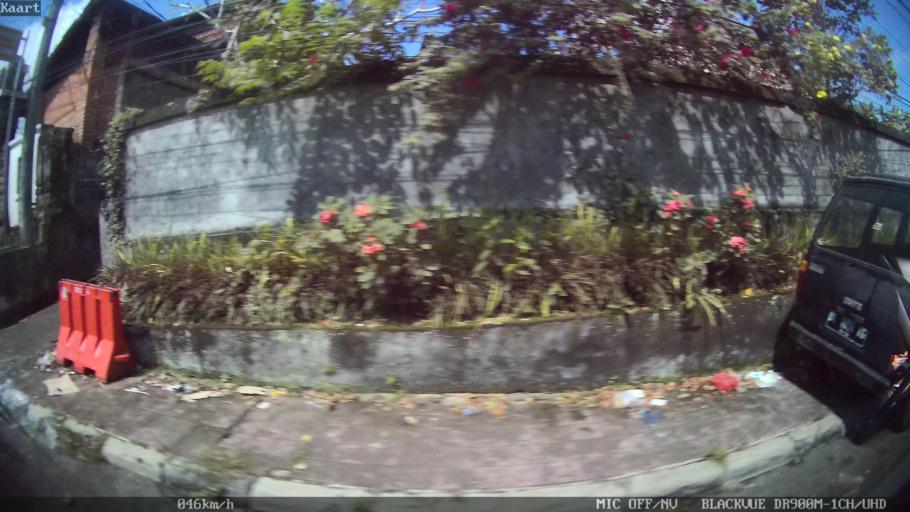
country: ID
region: Bali
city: Banjar Kelodan
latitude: -8.5279
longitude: 115.3288
